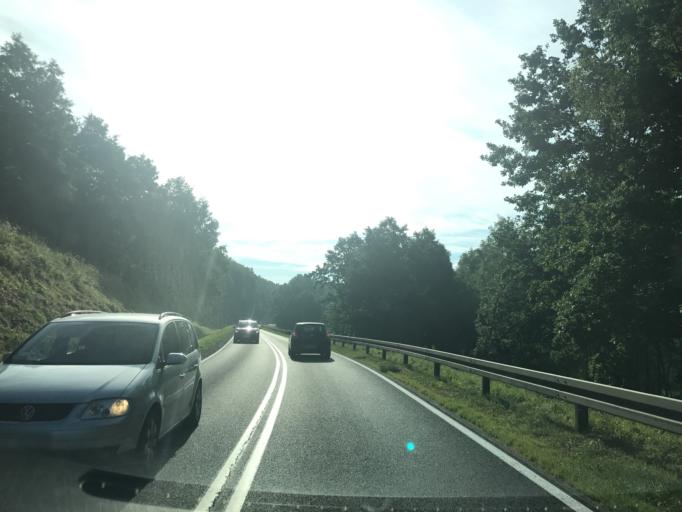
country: PL
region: West Pomeranian Voivodeship
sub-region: Powiat koszalinski
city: Bobolice
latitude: 53.9406
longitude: 16.6176
